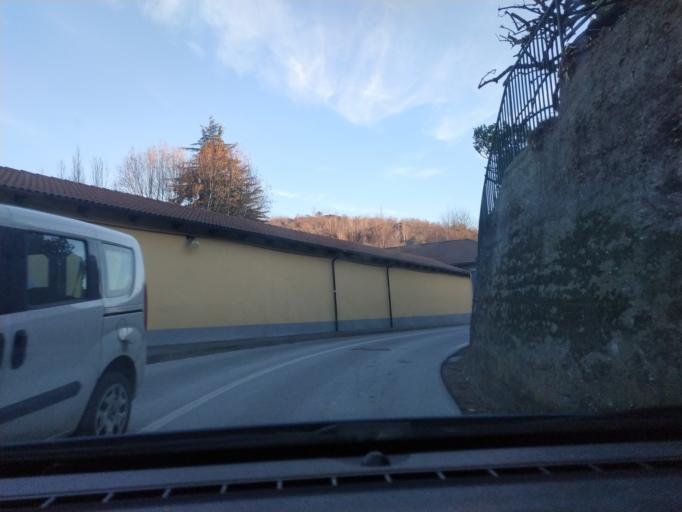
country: IT
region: Piedmont
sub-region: Provincia di Torino
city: Ivrea
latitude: 45.4824
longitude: 7.8786
